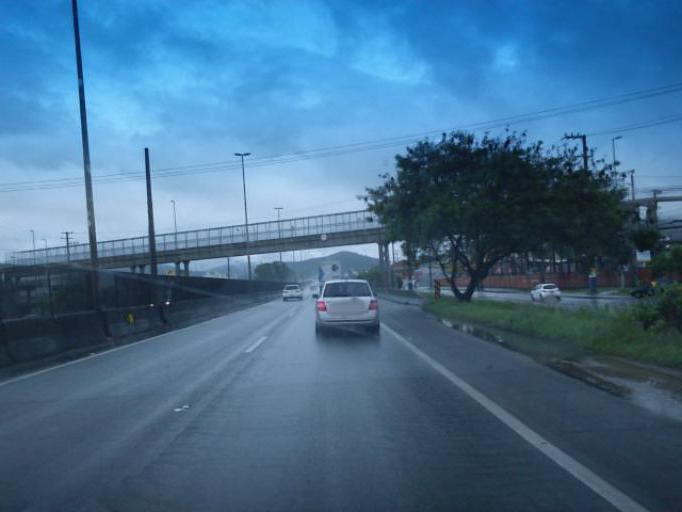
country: BR
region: Santa Catarina
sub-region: Balneario Camboriu
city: Balneario Camboriu
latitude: -27.0029
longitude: -48.6336
